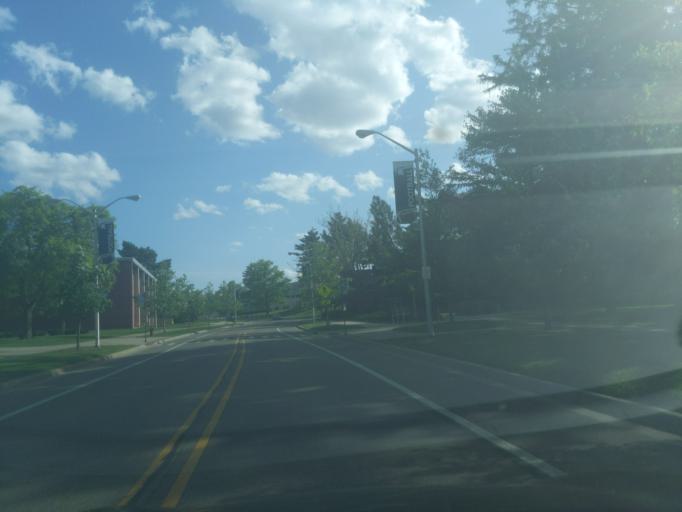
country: US
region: Michigan
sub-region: Ingham County
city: East Lansing
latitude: 42.7301
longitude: -84.4876
